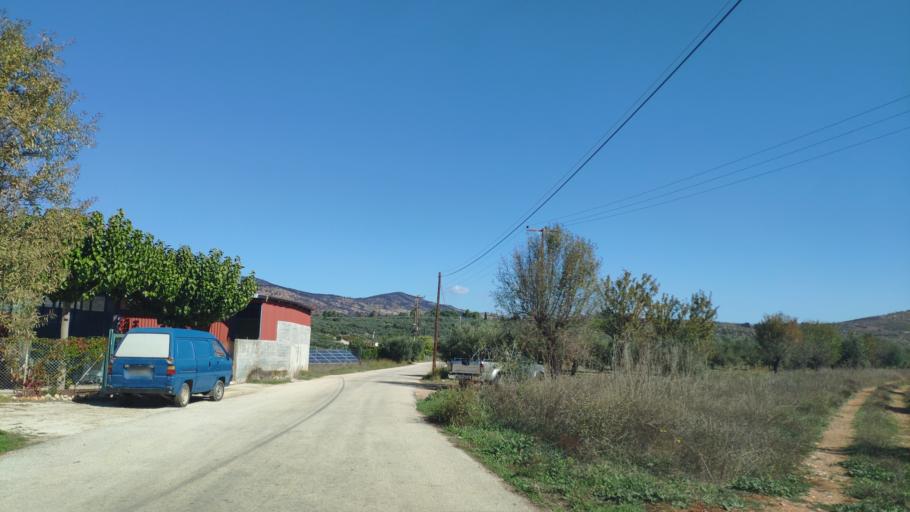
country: GR
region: Peloponnese
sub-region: Nomos Korinthias
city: Athikia
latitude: 37.8352
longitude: 22.9143
